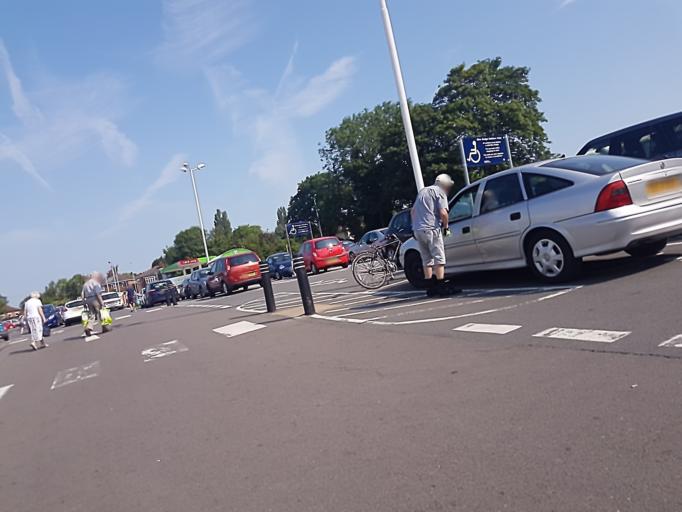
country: GB
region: England
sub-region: Leicestershire
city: Hinckley
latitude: 52.5516
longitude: -1.3634
